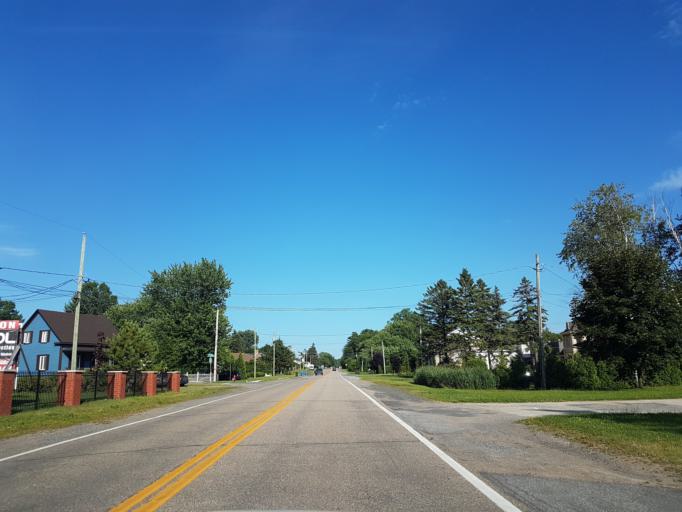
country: CA
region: Quebec
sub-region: Mauricie
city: Nicolet
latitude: 46.2862
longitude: -72.6884
